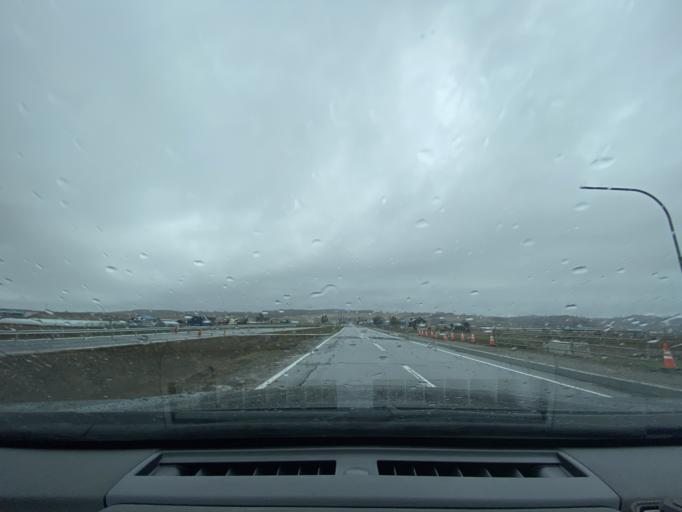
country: JP
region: Hokkaido
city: Fukagawa
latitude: 43.8064
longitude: 141.9114
